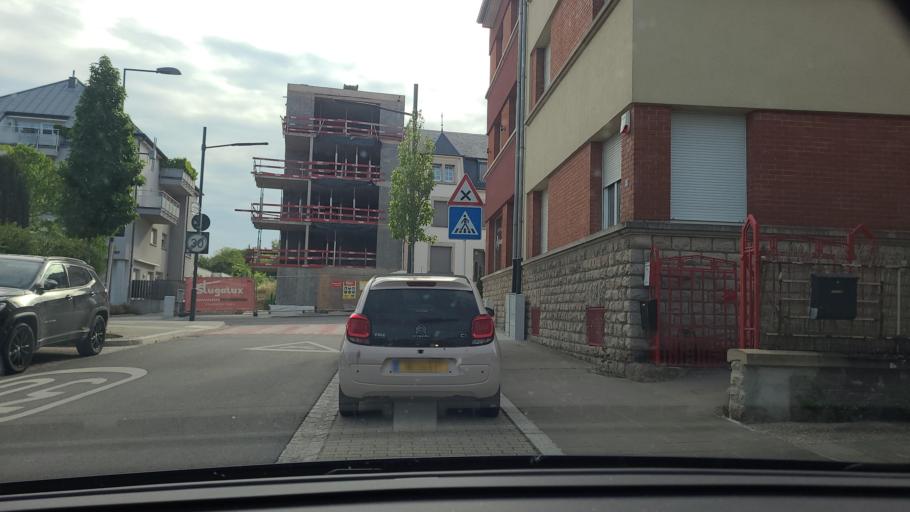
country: LU
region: Luxembourg
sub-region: Canton de Luxembourg
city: Luxembourg
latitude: 49.5979
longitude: 6.1495
